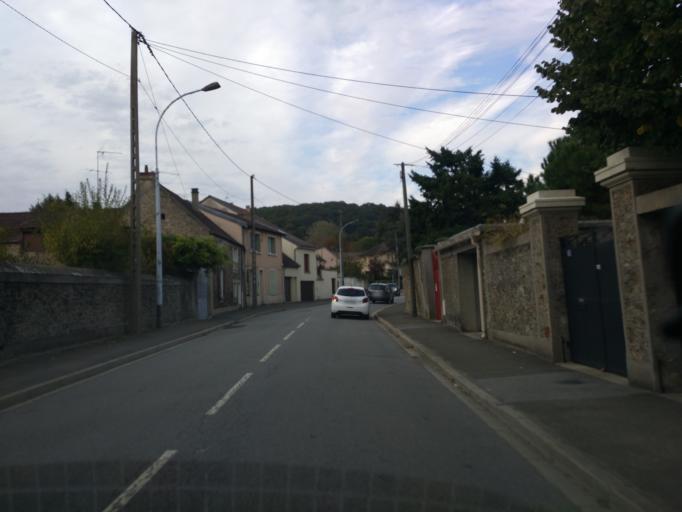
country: FR
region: Ile-de-France
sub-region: Departement des Yvelines
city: Chevreuse
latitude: 48.7055
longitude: 2.0377
